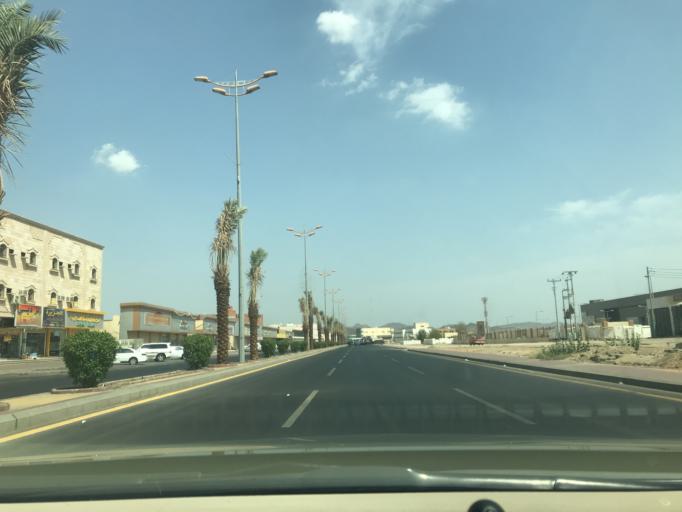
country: SA
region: Makkah
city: Al Jumum
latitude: 21.6183
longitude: 39.6884
